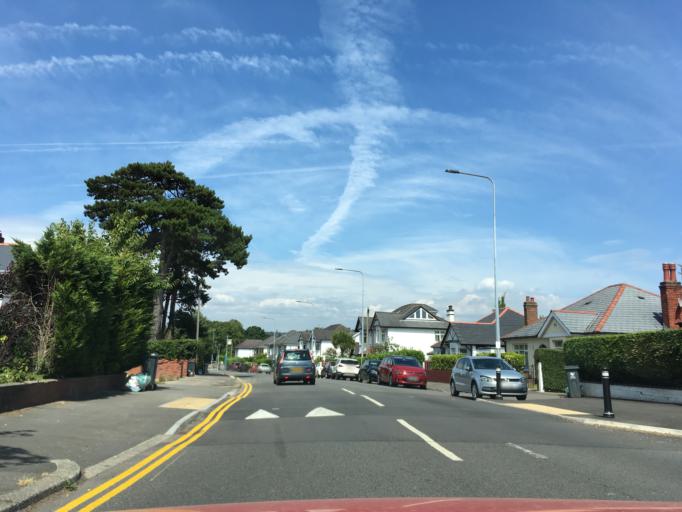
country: GB
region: Wales
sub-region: Cardiff
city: Cardiff
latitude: 51.5123
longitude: -3.1817
